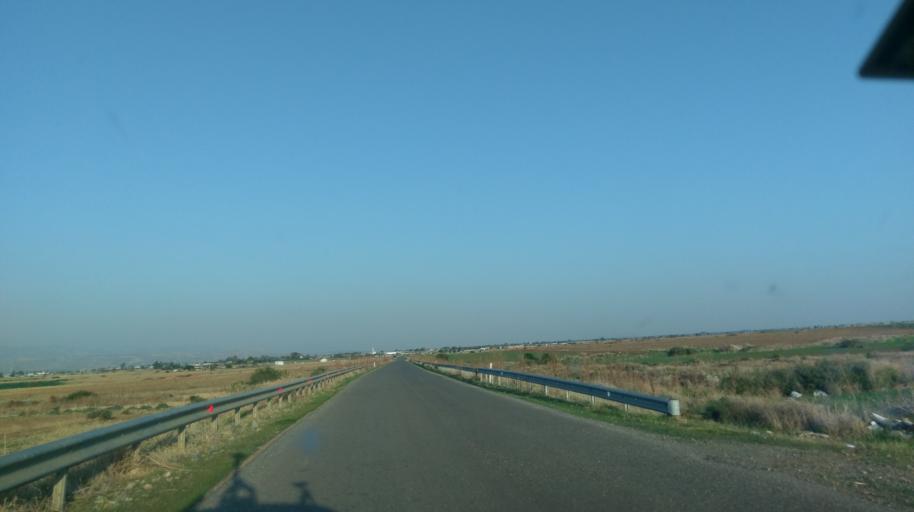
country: CY
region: Lefkosia
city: Morfou
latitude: 35.1513
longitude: 32.9834
